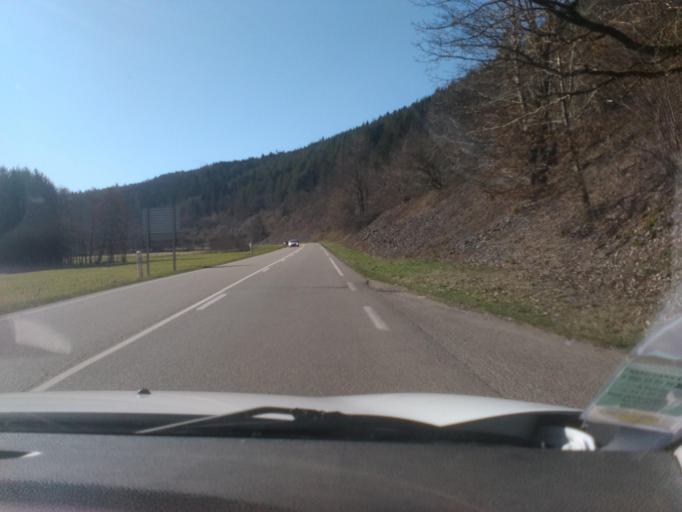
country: FR
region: Alsace
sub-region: Departement du Bas-Rhin
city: Rothau
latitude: 48.4444
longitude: 7.1931
